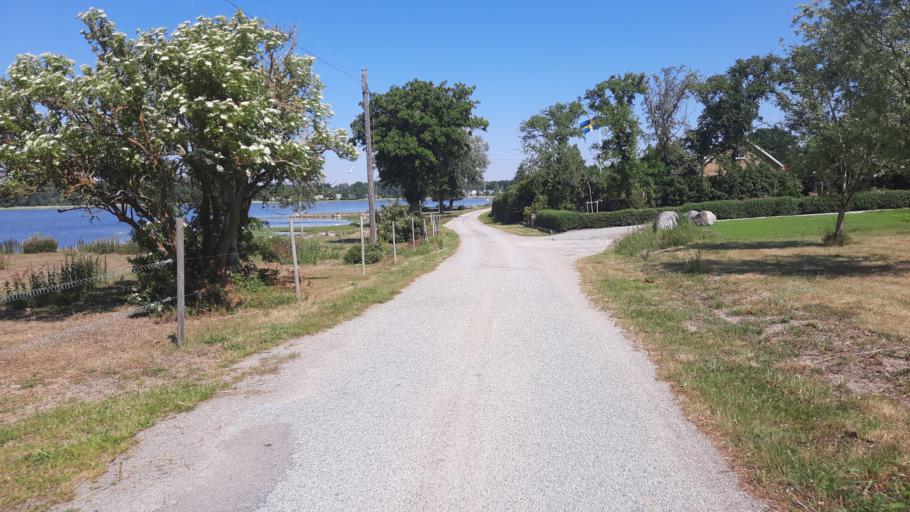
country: SE
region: Blekinge
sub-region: Karlskrona Kommun
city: Jaemjoe
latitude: 56.1548
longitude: 15.7587
